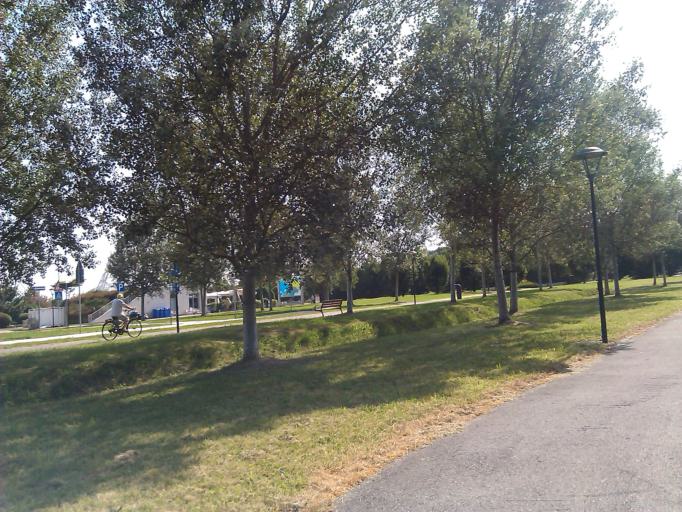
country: IT
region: Veneto
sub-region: Provincia di Venezia
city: Campalto
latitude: 45.4771
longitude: 12.2702
